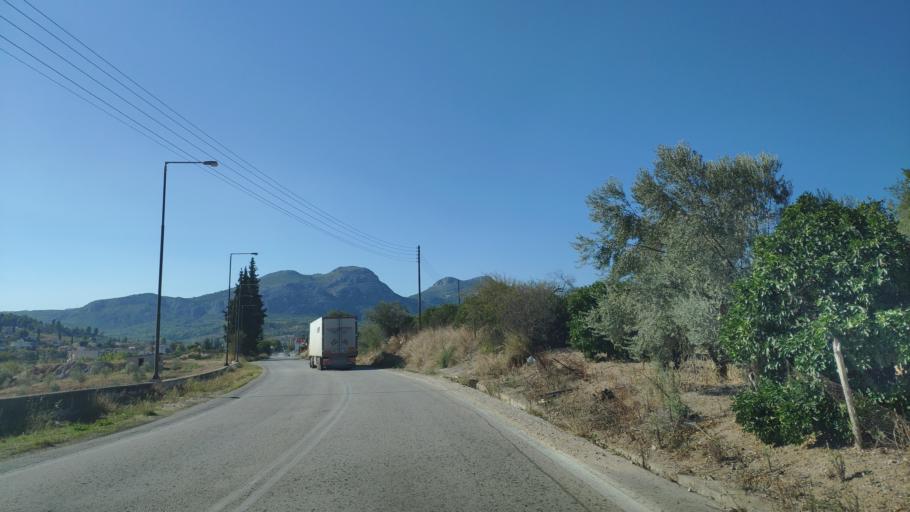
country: GR
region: Peloponnese
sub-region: Nomos Korinthias
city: Arkhaia Korinthos
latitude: 37.8847
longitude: 22.8931
